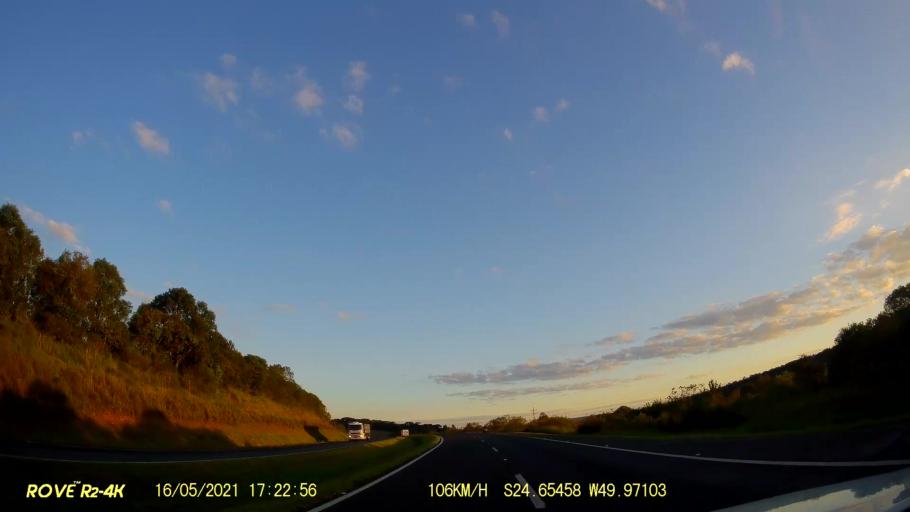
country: BR
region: Parana
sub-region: Pirai Do Sul
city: Pirai do Sul
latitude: -24.6547
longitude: -49.9713
